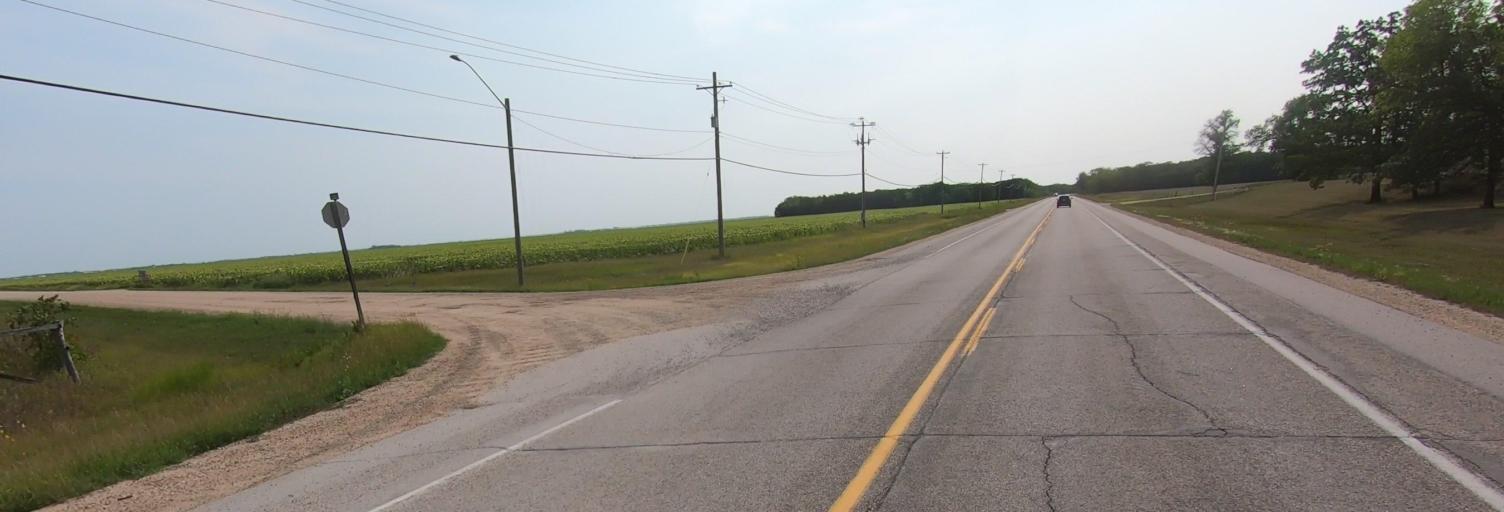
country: CA
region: Manitoba
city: Niverville
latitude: 49.7332
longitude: -97.1022
